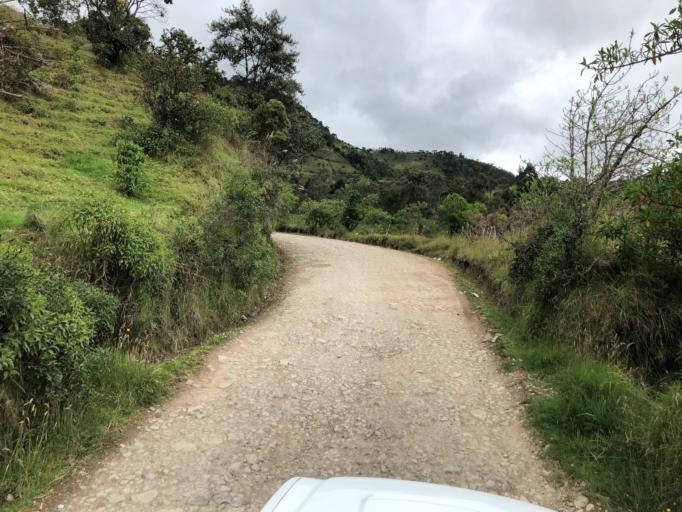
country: CO
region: Cauca
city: Totoro
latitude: 2.5093
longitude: -76.3655
